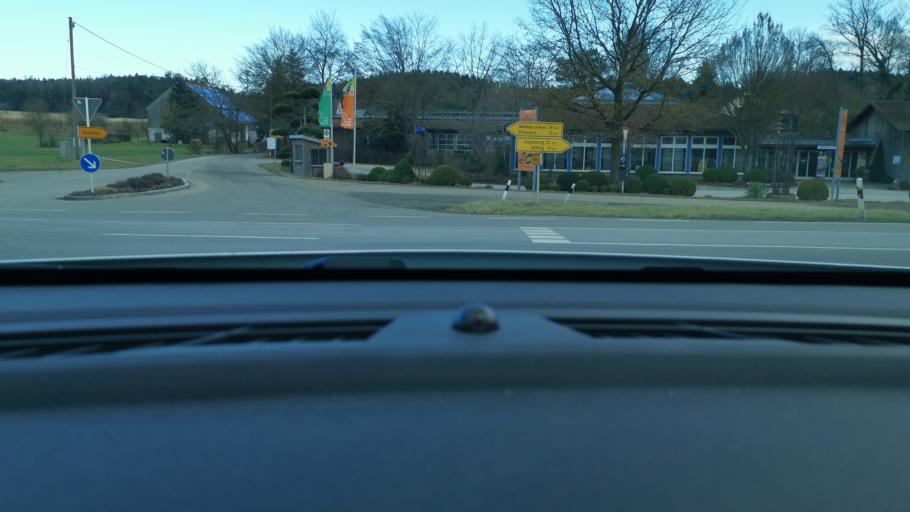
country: DE
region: Bavaria
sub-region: Swabia
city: Petersdorf
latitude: 48.4934
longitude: 11.0097
